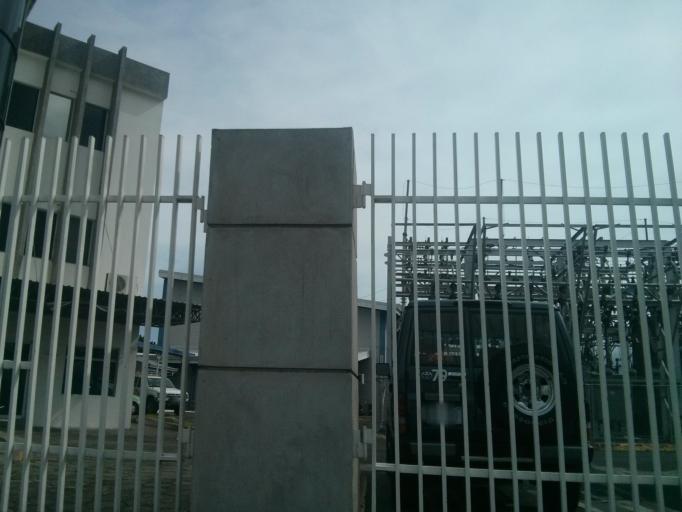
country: CR
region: San Jose
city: Colima
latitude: 9.9479
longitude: -84.0920
